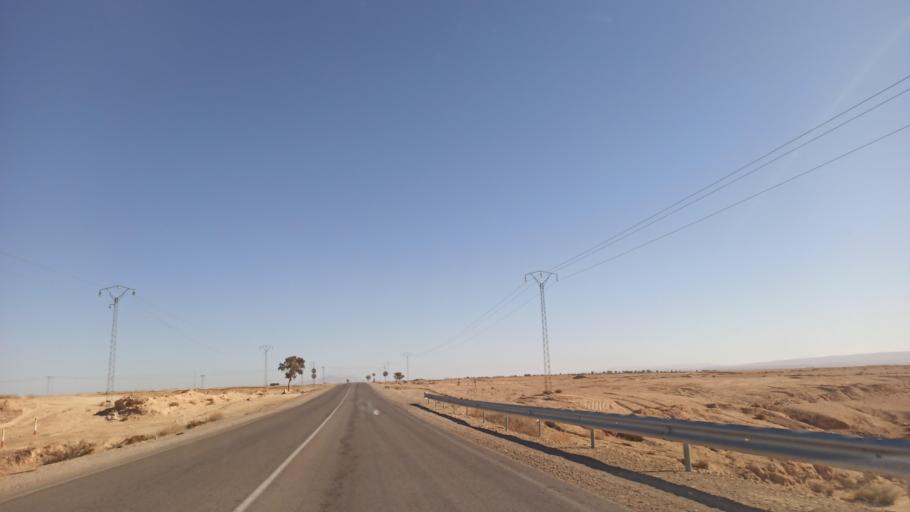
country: TN
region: Gafsa
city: Al Metlaoui
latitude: 34.3119
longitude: 8.4753
